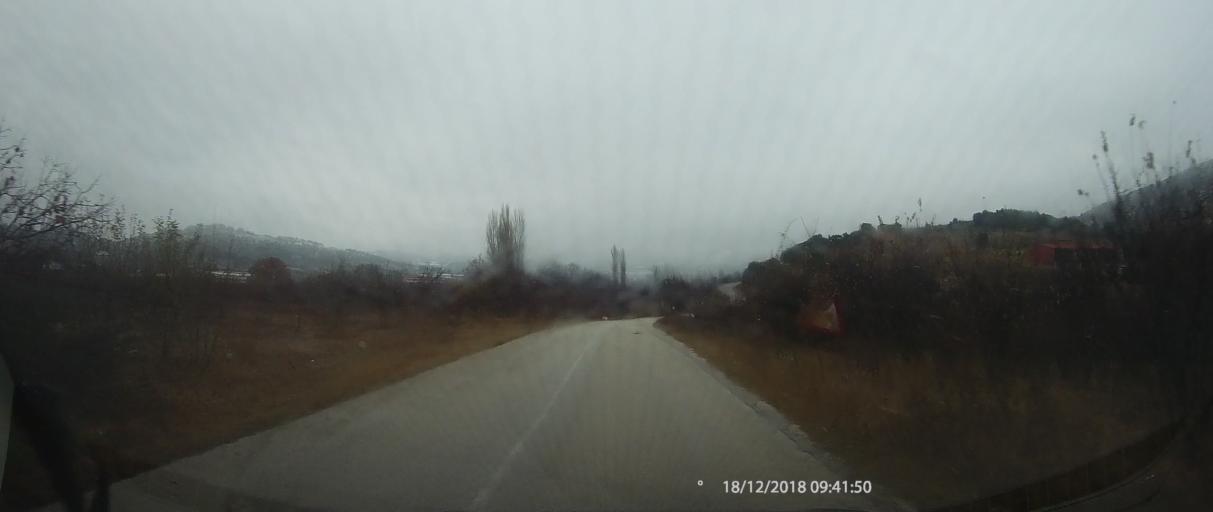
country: GR
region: Thessaly
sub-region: Nomos Larisis
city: Elassona
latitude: 40.0157
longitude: 22.2334
